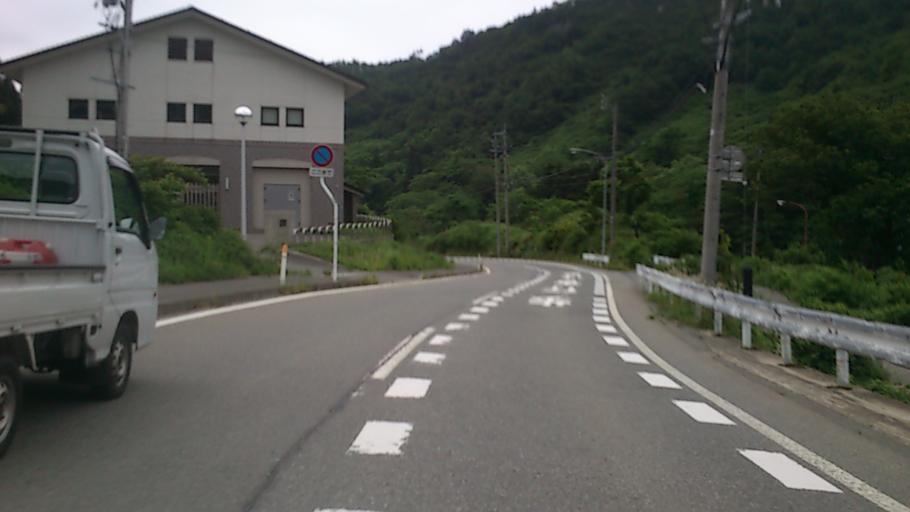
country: JP
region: Yamagata
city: Obanazawa
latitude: 38.5734
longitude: 140.5251
